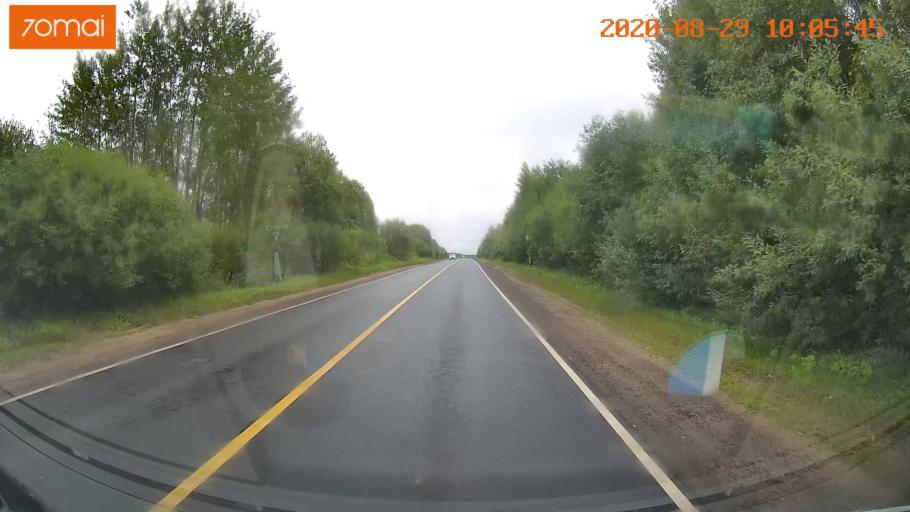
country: RU
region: Ivanovo
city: Zarechnyy
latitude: 57.3919
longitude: 42.5294
